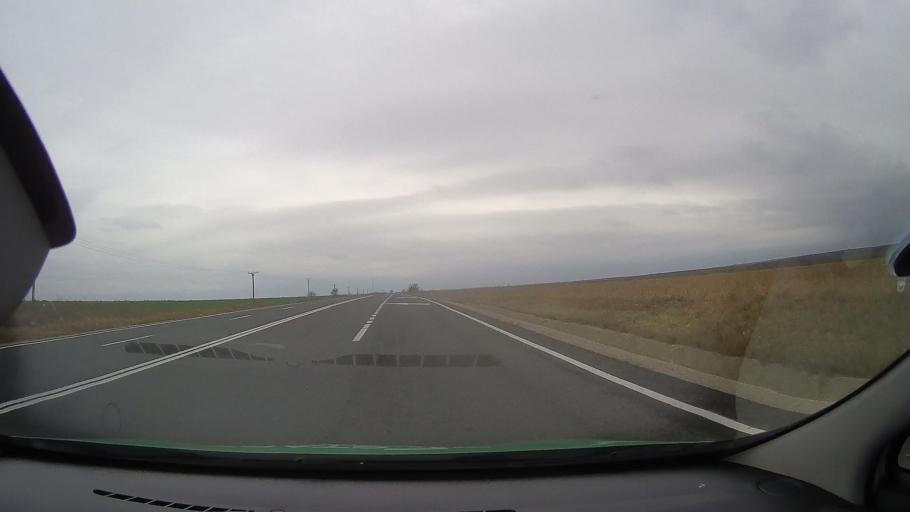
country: RO
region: Constanta
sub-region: Comuna Nicolae Balcescu
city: Nicolae Balcescu
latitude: 44.3803
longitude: 28.4081
